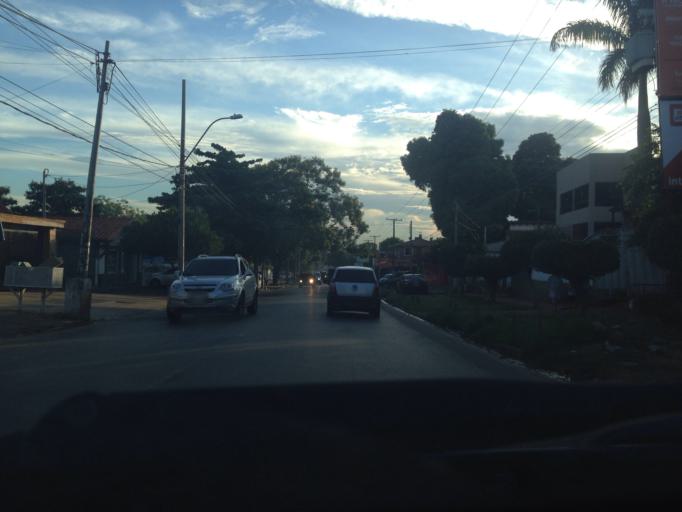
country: PY
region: Central
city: Lambare
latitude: -25.3297
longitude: -57.5858
